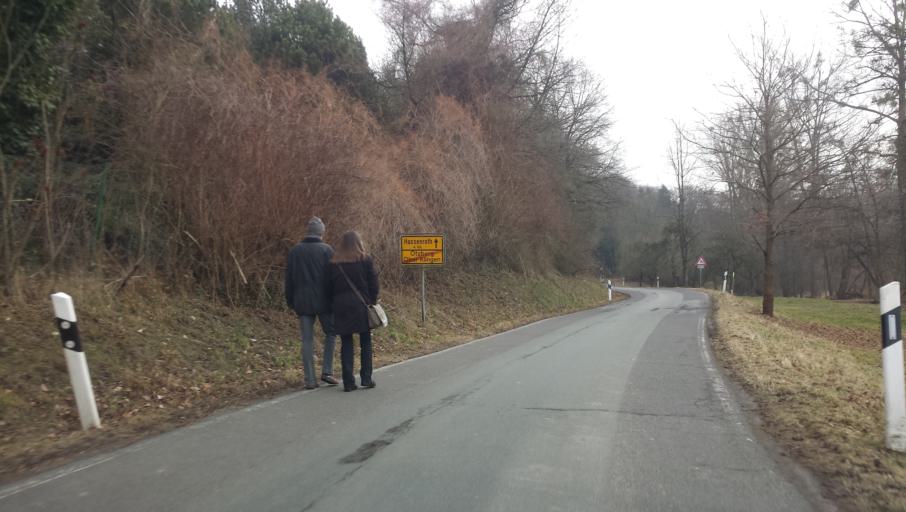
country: DE
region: Hesse
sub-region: Regierungsbezirk Darmstadt
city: Brensbach
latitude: 49.8079
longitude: 8.8995
